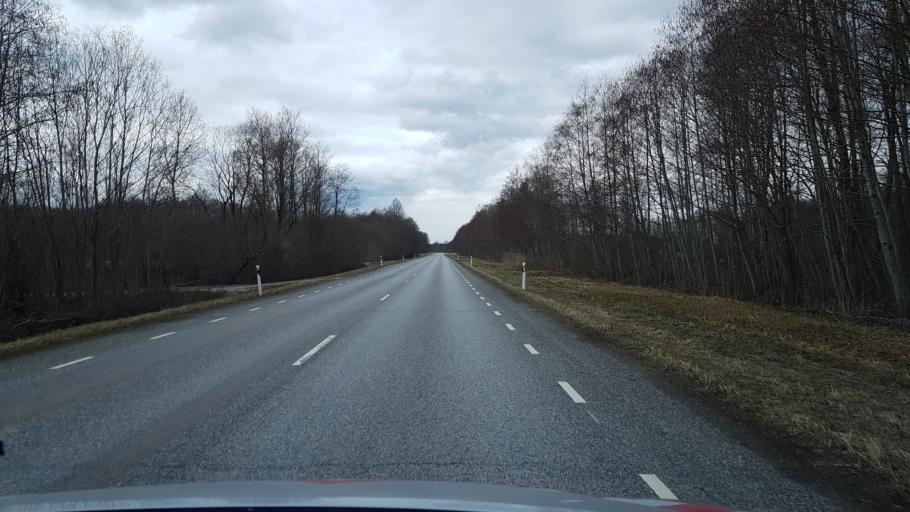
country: EE
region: Ida-Virumaa
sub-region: Narva-Joesuu linn
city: Narva-Joesuu
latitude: 59.3461
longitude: 28.0124
